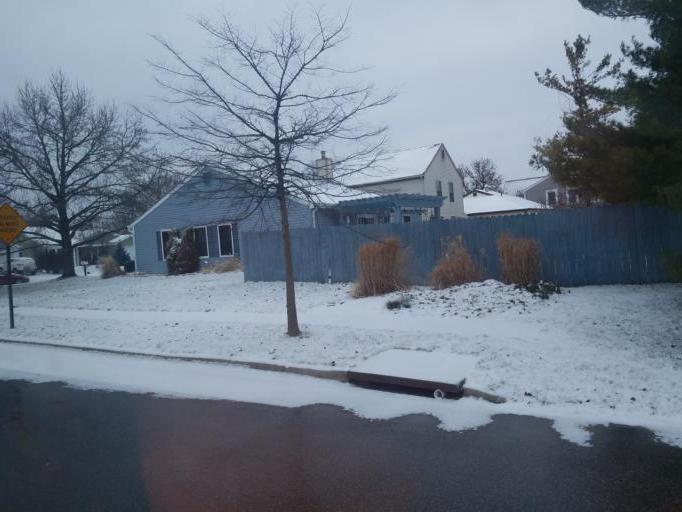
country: US
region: Ohio
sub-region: Delaware County
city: Powell
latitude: 40.1148
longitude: -83.0669
